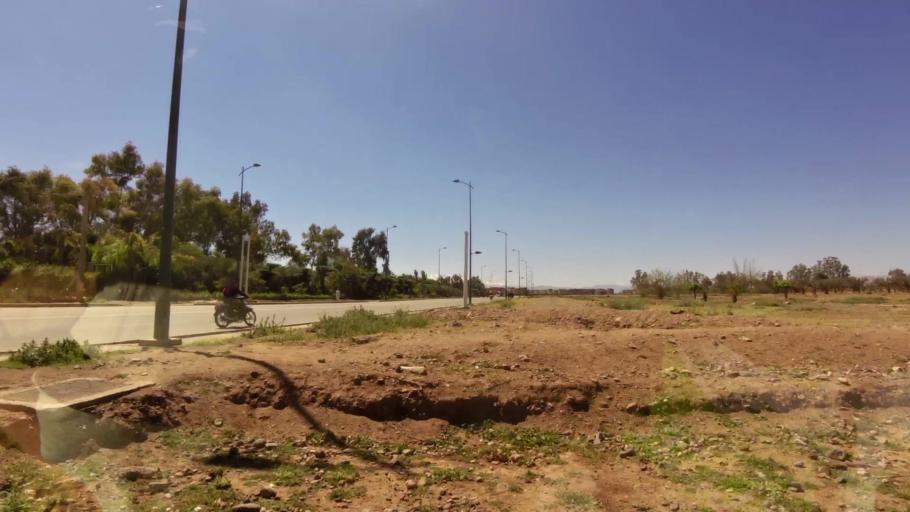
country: MA
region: Marrakech-Tensift-Al Haouz
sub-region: Marrakech
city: Marrakesh
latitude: 31.5699
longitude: -7.9807
